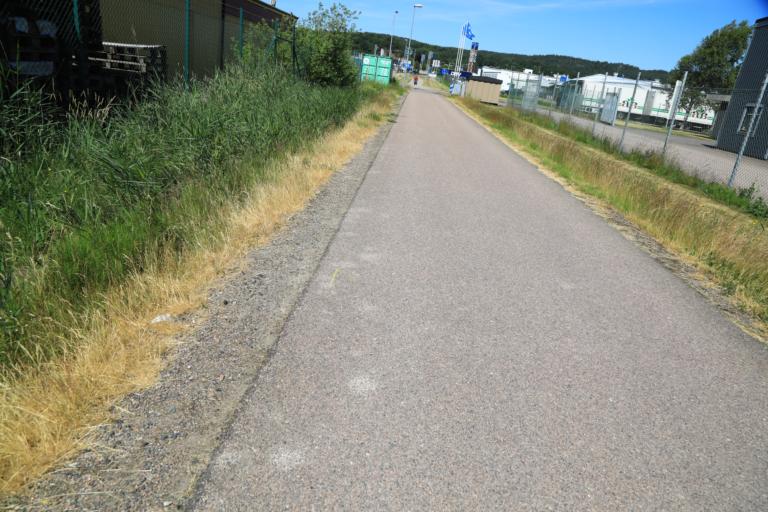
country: SE
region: Halland
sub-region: Kungsbacka Kommun
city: Kungsbacka
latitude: 57.5093
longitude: 12.0737
